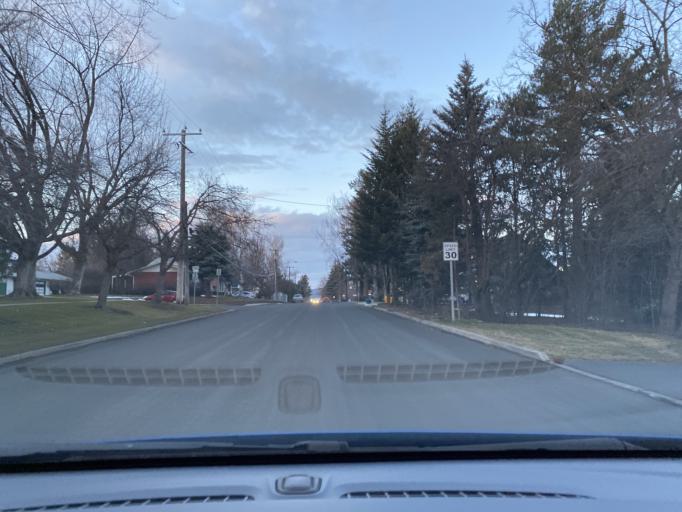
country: US
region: Idaho
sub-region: Latah County
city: Moscow
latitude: 46.7407
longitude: -116.9855
